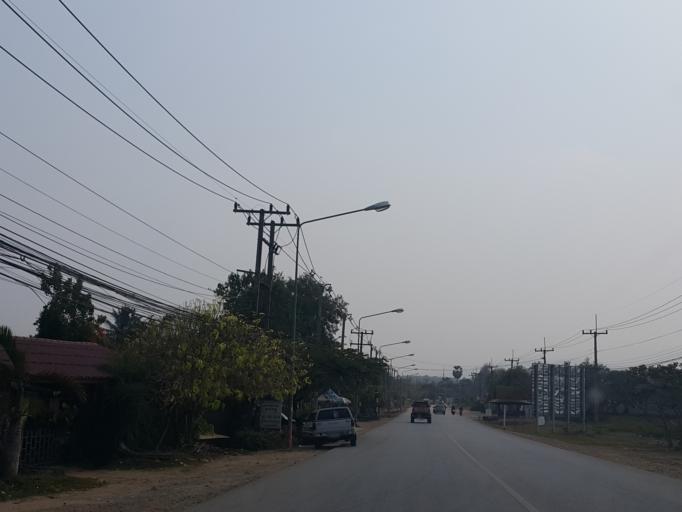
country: TH
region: Chiang Mai
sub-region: Amphoe Chiang Dao
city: Chiang Dao
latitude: 19.3600
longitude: 98.9644
